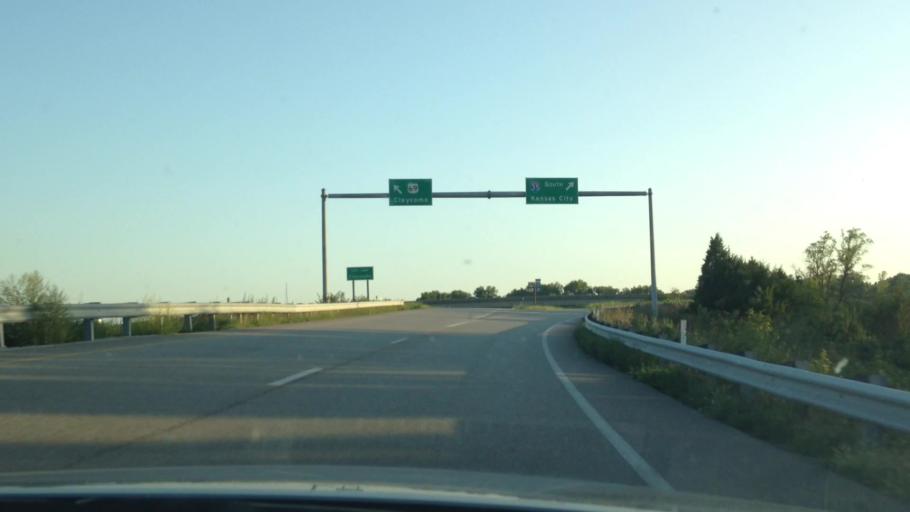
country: US
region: Missouri
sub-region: Clay County
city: Claycomo
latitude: 39.2084
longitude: -94.4918
